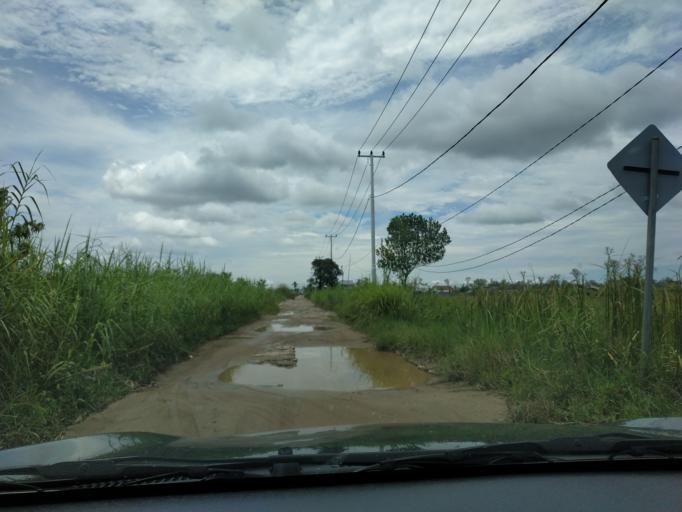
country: ID
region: Riau
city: Tembilahan
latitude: -0.3086
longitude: 103.1838
